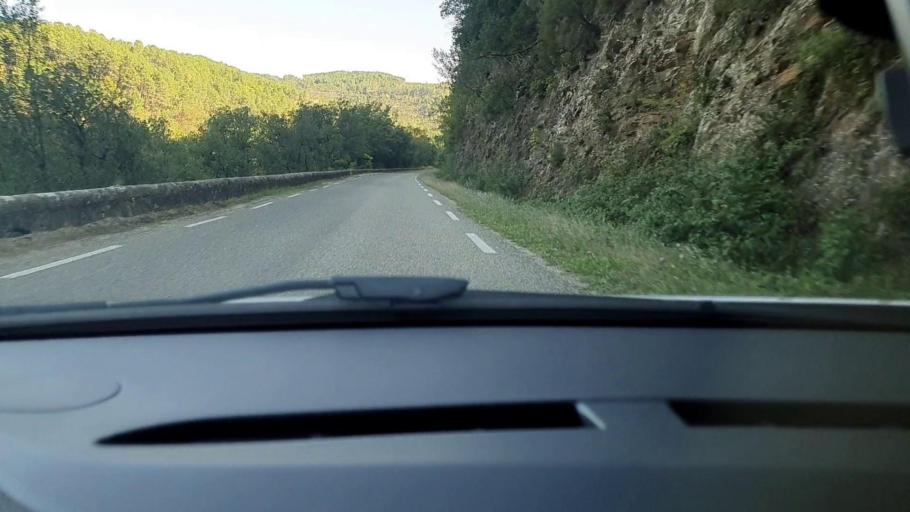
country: FR
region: Languedoc-Roussillon
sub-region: Departement du Gard
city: Besseges
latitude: 44.2896
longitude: 4.0719
